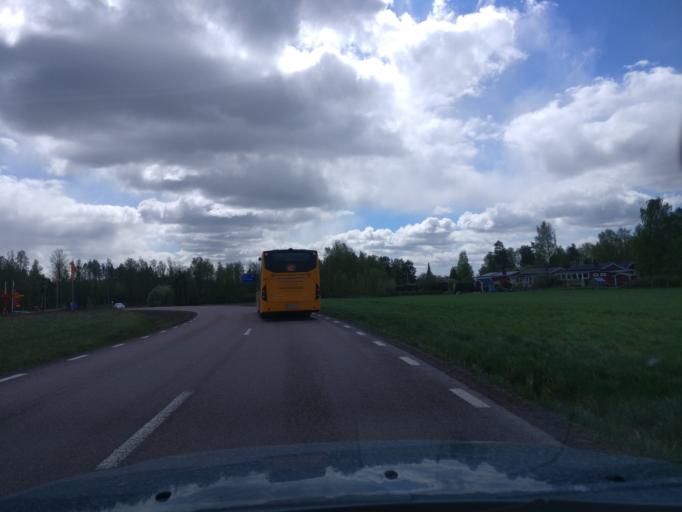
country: SE
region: Vaermland
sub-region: Karlstads Kommun
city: Molkom
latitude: 59.6055
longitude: 13.7386
